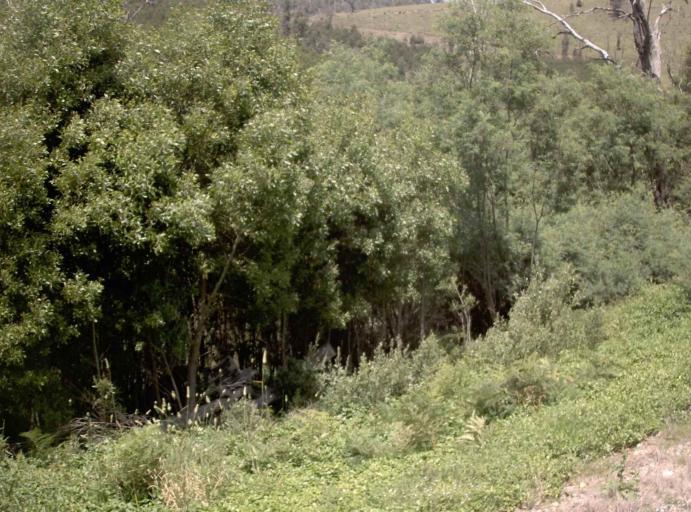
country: AU
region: Victoria
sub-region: East Gippsland
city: Bairnsdale
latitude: -37.5243
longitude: 147.8444
